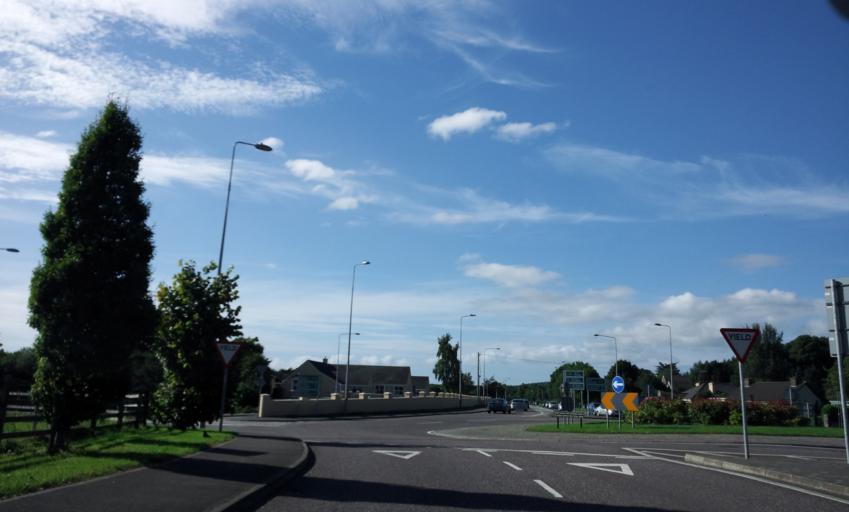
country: IE
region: Munster
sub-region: Ciarrai
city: Cill Airne
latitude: 52.0504
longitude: -9.4571
